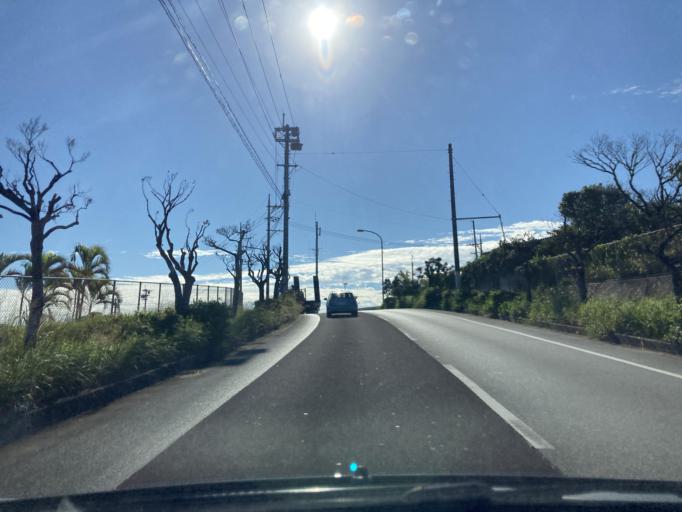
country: JP
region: Okinawa
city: Okinawa
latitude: 26.3693
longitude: 127.7713
